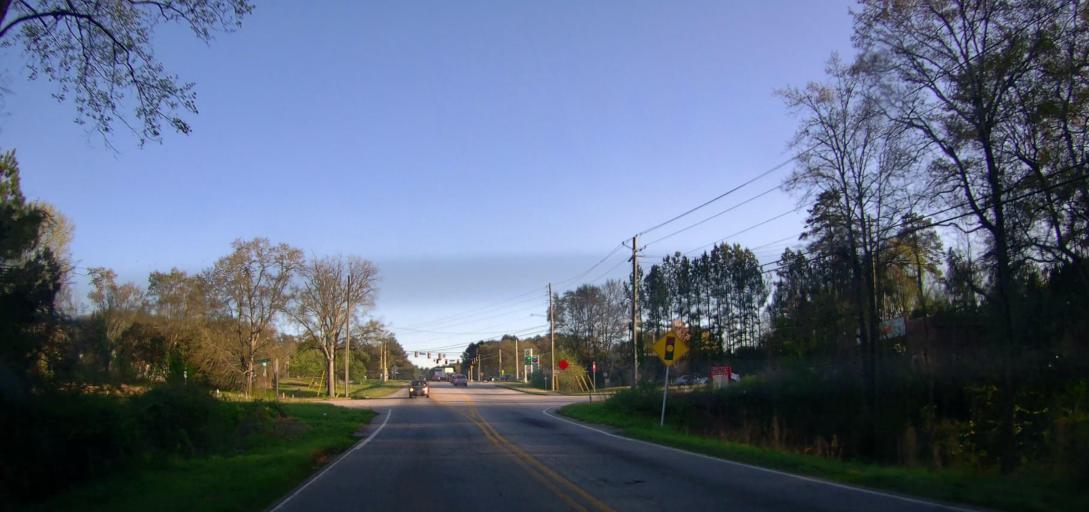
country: US
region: Georgia
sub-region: Newton County
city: Porterdale
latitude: 33.5671
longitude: -83.9027
